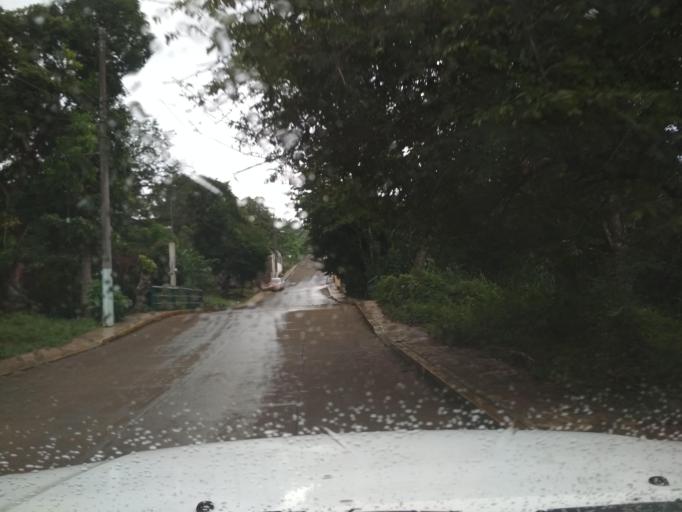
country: MX
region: Veracruz
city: San Andres Tuxtla
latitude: 18.4553
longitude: -95.2255
